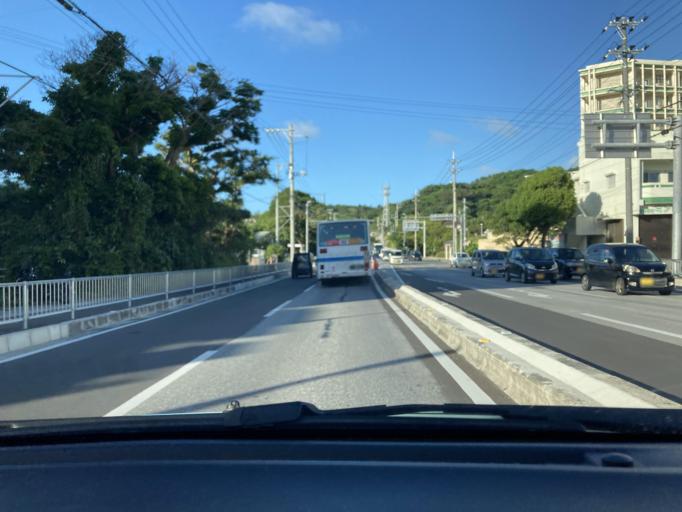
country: JP
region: Okinawa
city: Naha-shi
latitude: 26.2053
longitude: 127.7222
